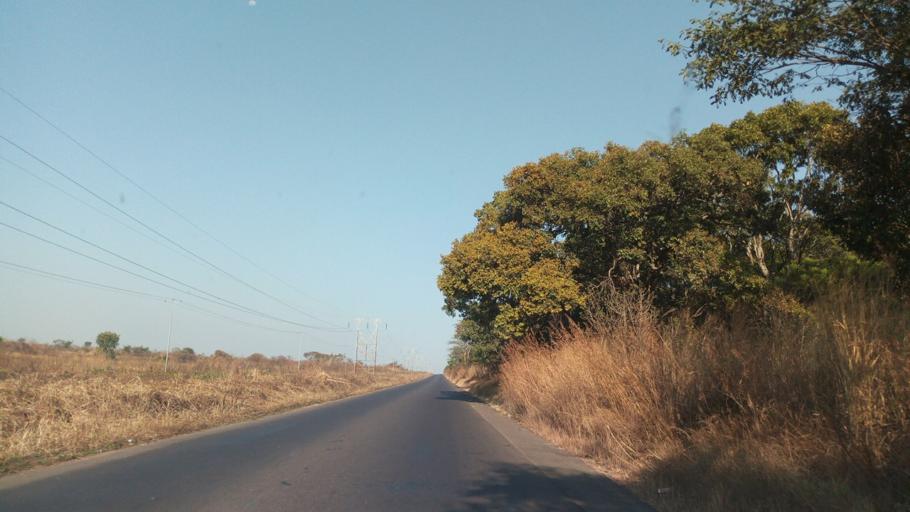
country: CD
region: Katanga
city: Likasi
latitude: -11.0047
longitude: 26.9012
